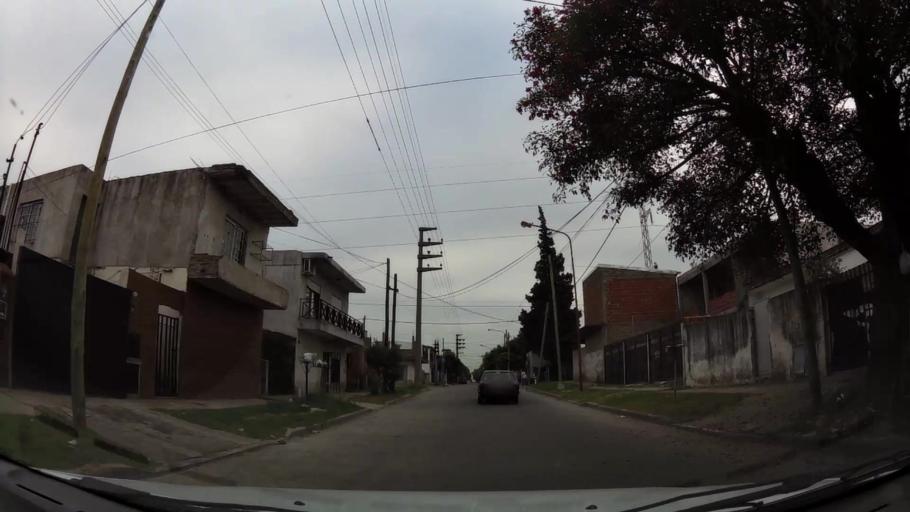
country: AR
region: Buenos Aires
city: San Justo
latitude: -34.7042
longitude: -58.5696
